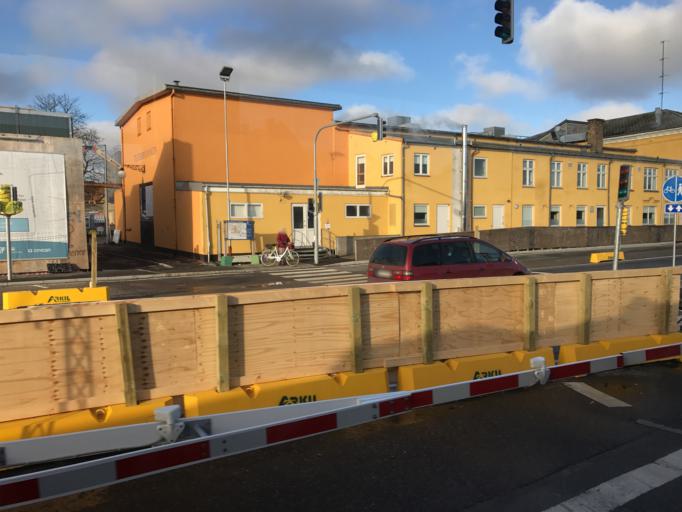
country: DK
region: Zealand
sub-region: Koge Kommune
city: Koge
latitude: 55.4554
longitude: 12.1856
